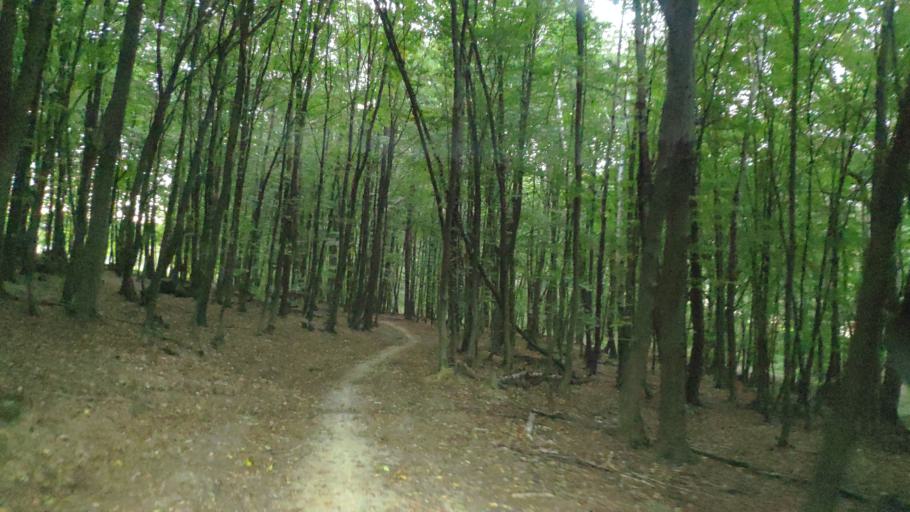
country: SK
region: Kosicky
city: Kosice
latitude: 48.7024
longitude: 21.1944
